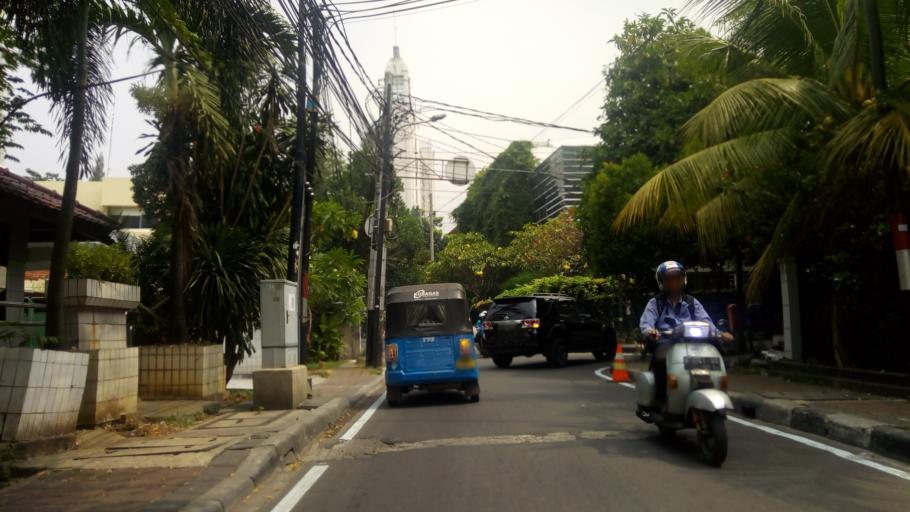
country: ID
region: Jakarta Raya
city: Jakarta
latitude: -6.1930
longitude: 106.8382
